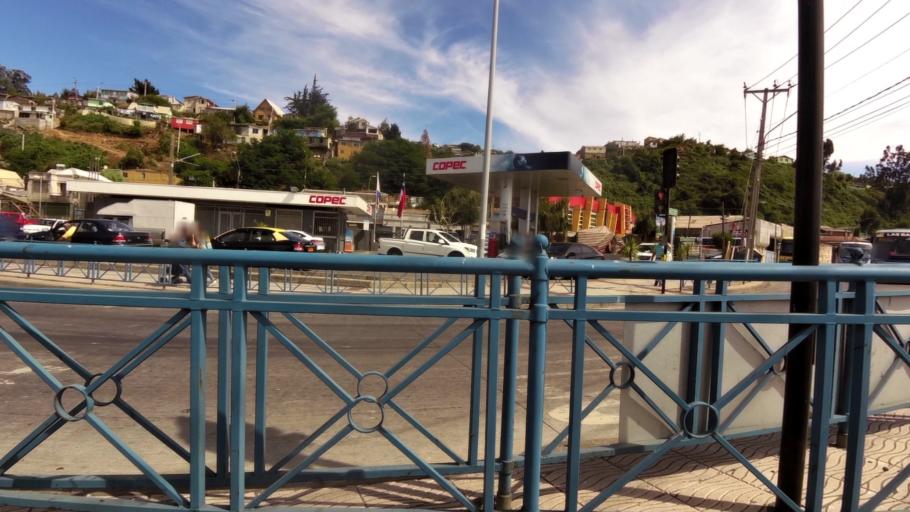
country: CL
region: Biobio
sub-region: Provincia de Concepcion
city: Talcahuano
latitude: -36.7116
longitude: -73.1148
